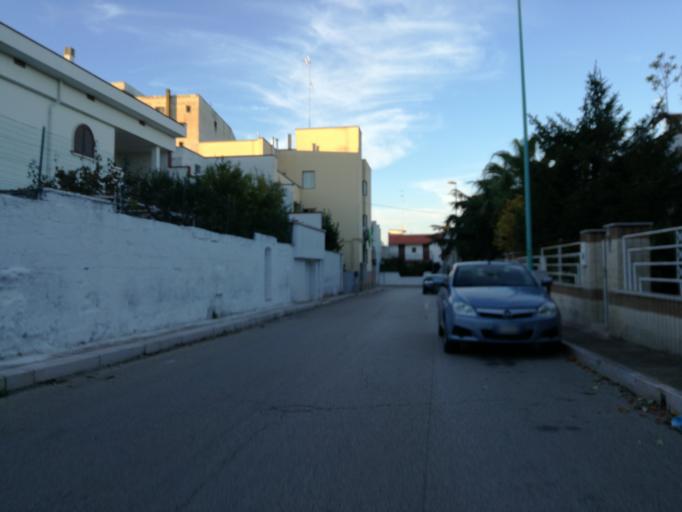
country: IT
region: Apulia
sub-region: Provincia di Bari
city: Adelfia
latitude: 41.0032
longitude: 16.8813
